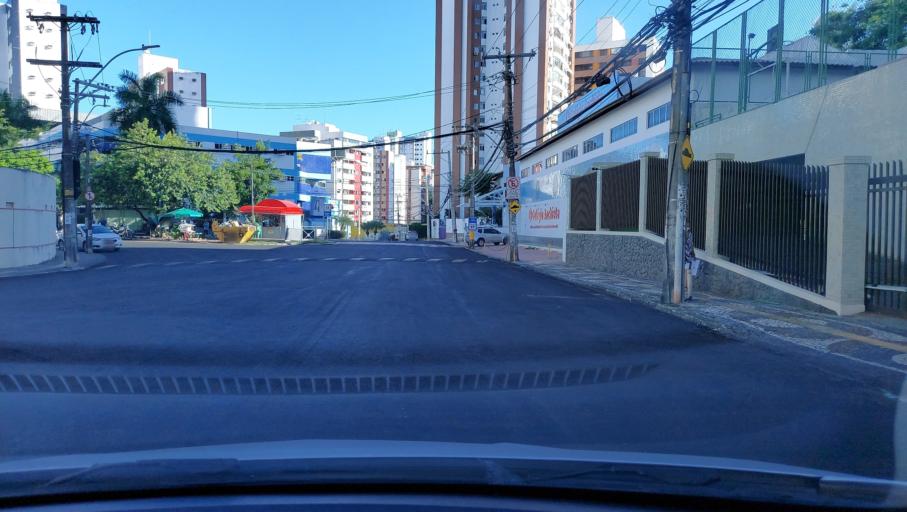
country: BR
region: Bahia
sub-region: Salvador
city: Salvador
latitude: -12.9887
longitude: -38.4531
